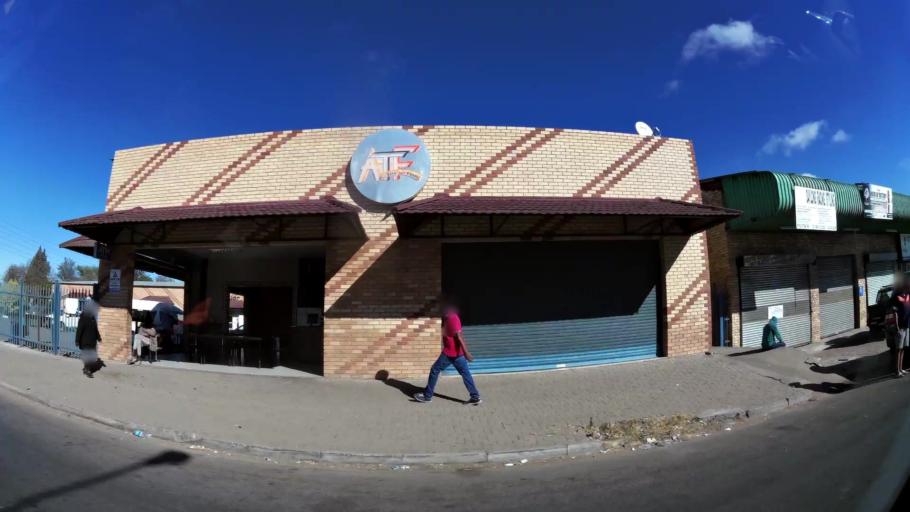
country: ZA
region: Limpopo
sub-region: Capricorn District Municipality
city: Polokwane
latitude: -23.8817
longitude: 29.4426
